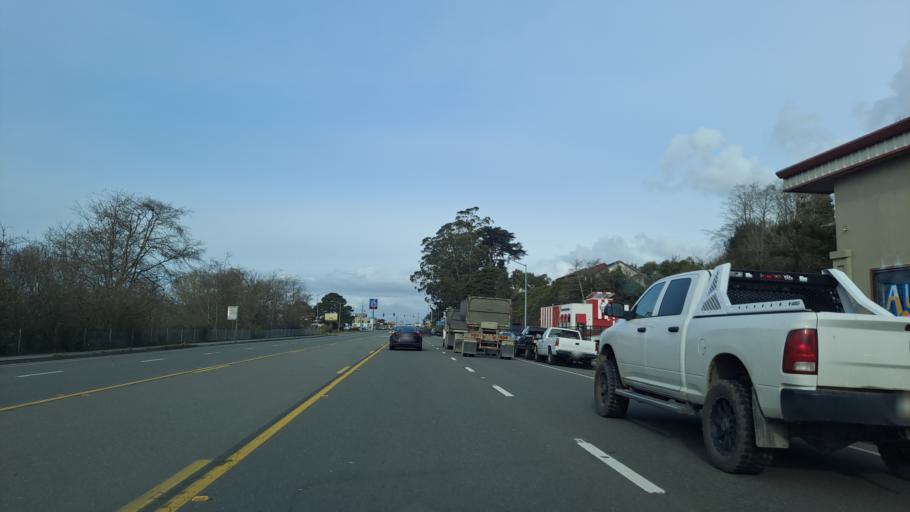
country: US
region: California
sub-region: Humboldt County
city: Bayview
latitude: 40.7864
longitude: -124.1813
